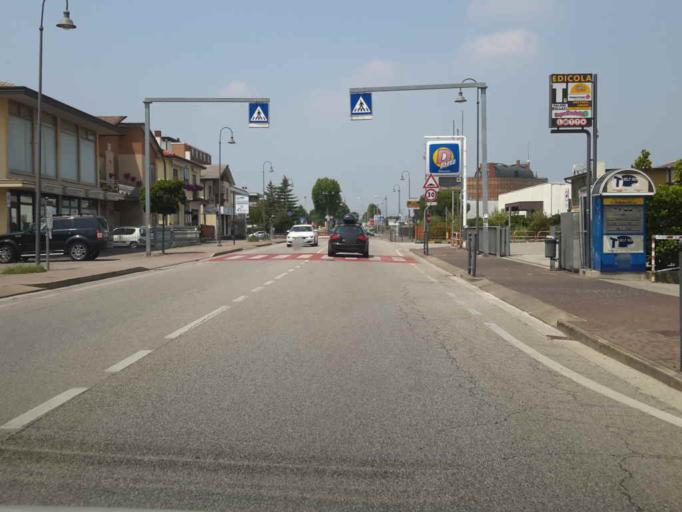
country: IT
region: Veneto
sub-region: Provincia di Vicenza
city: Torri di Quartesolo
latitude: 45.5226
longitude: 11.6107
